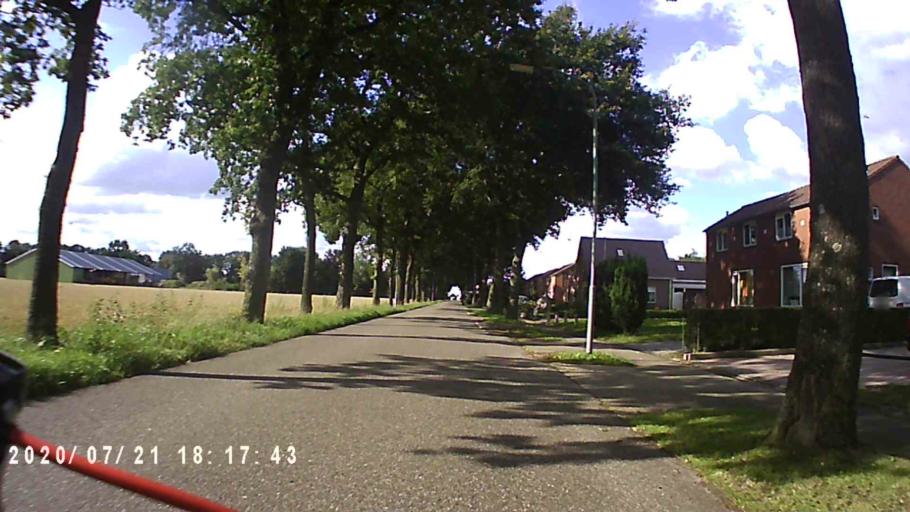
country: NL
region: Groningen
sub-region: Gemeente Hoogezand-Sappemeer
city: Hoogezand
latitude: 53.1807
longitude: 6.7548
